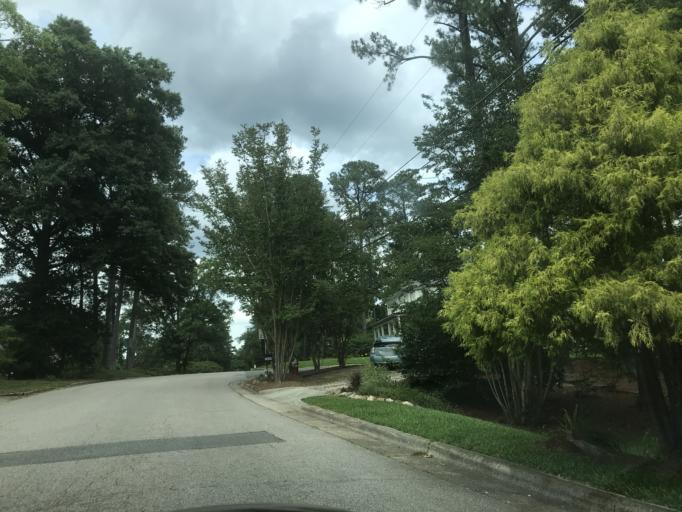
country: US
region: North Carolina
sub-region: Wake County
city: West Raleigh
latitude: 35.8297
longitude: -78.6385
